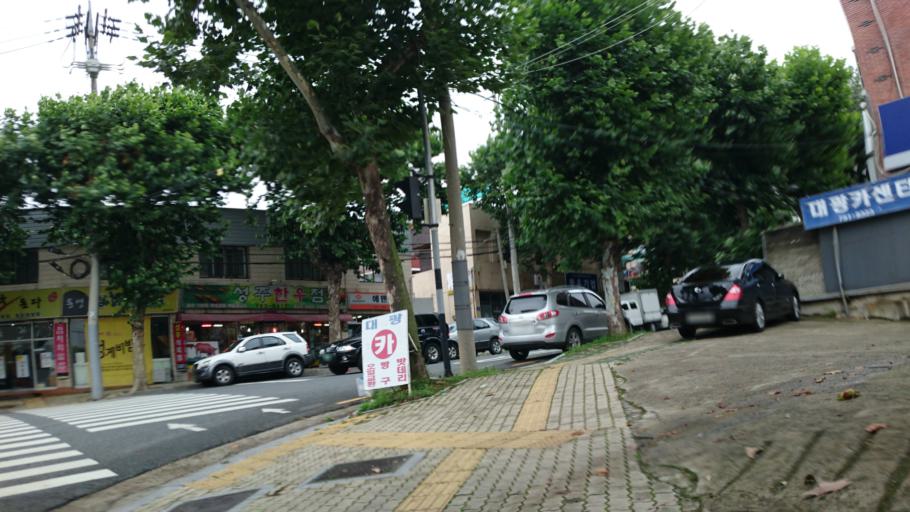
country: KR
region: Daegu
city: Daegu
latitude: 35.8683
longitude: 128.6462
